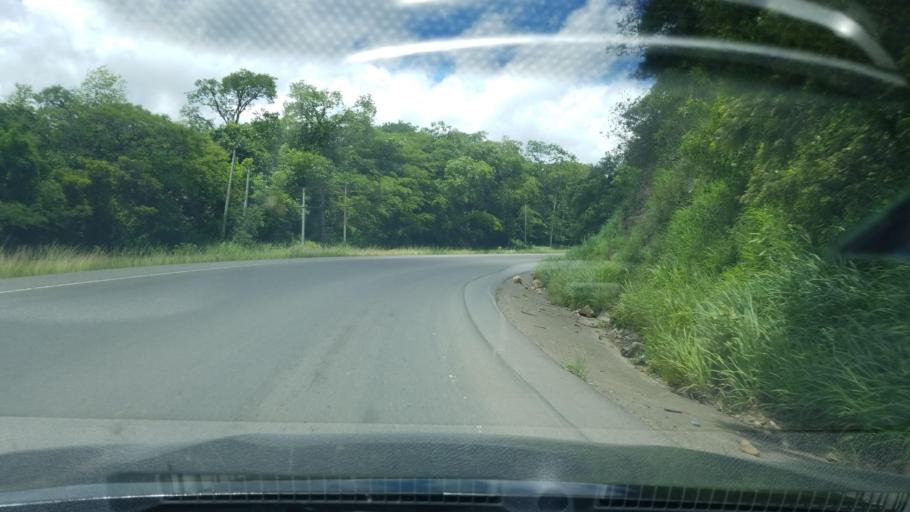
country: HN
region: Francisco Morazan
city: Rio Abajo
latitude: 14.1835
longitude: -87.2038
